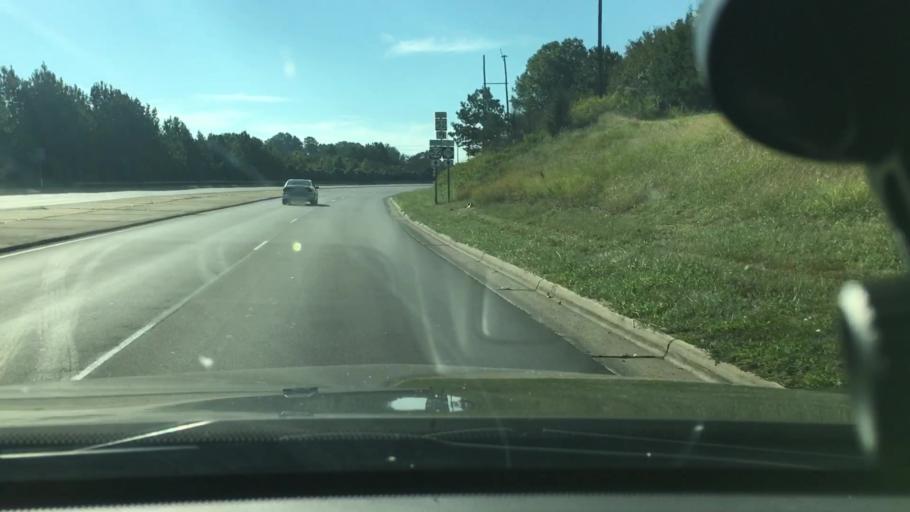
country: US
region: North Carolina
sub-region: Stanly County
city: Albemarle
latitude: 35.3416
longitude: -80.2011
